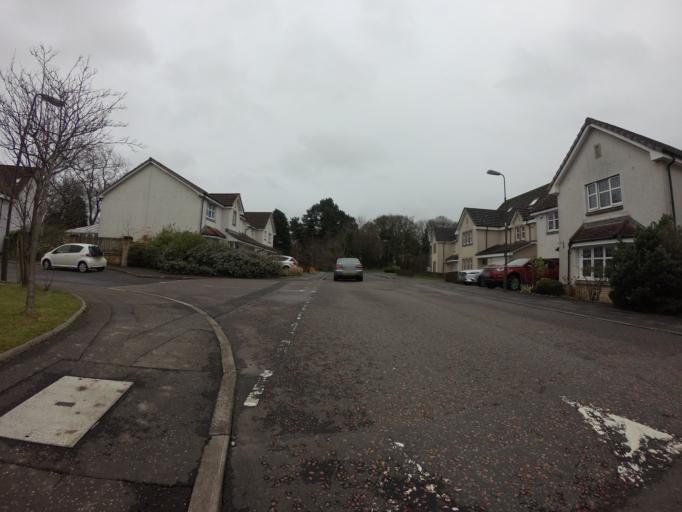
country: GB
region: Scotland
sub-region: West Lothian
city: Livingston
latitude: 55.9061
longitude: -3.5688
